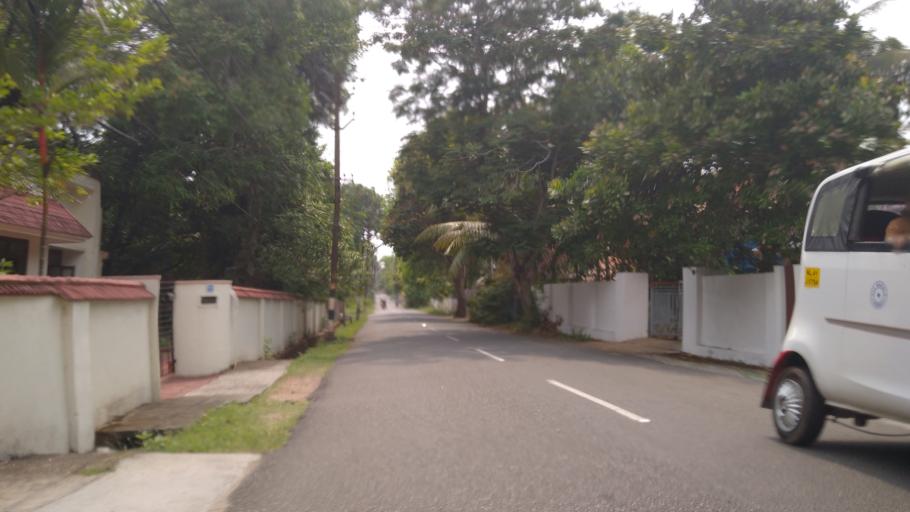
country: IN
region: Kerala
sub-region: Ernakulam
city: Elur
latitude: 10.1456
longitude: 76.2502
